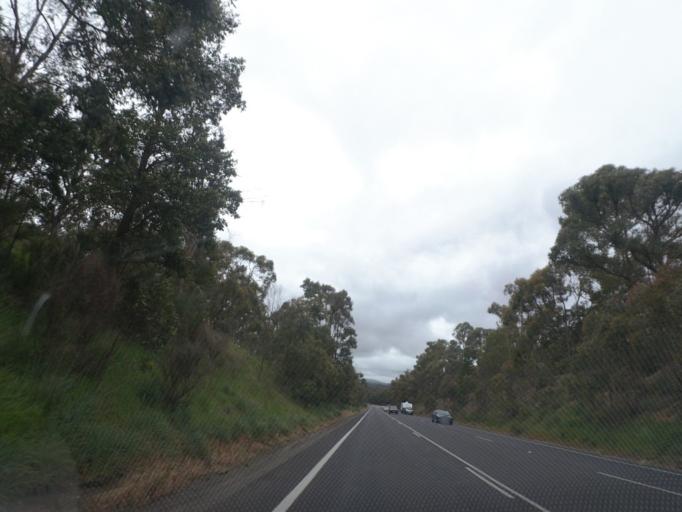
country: AU
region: Victoria
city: Brown Hill
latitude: -37.4466
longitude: 143.8851
